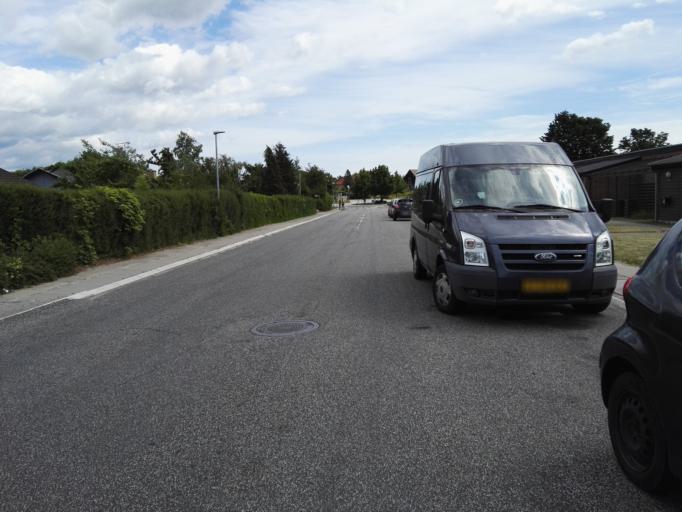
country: DK
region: Capital Region
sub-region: Egedal Kommune
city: Stenlose
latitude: 55.7709
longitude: 12.1928
